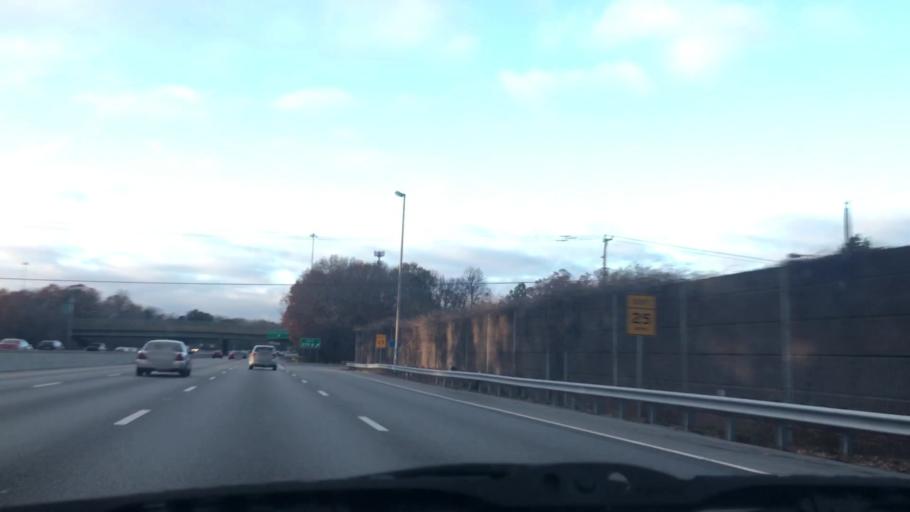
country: US
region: Virginia
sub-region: City of Norfolk
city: Norfolk
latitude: 36.8893
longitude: -76.2295
